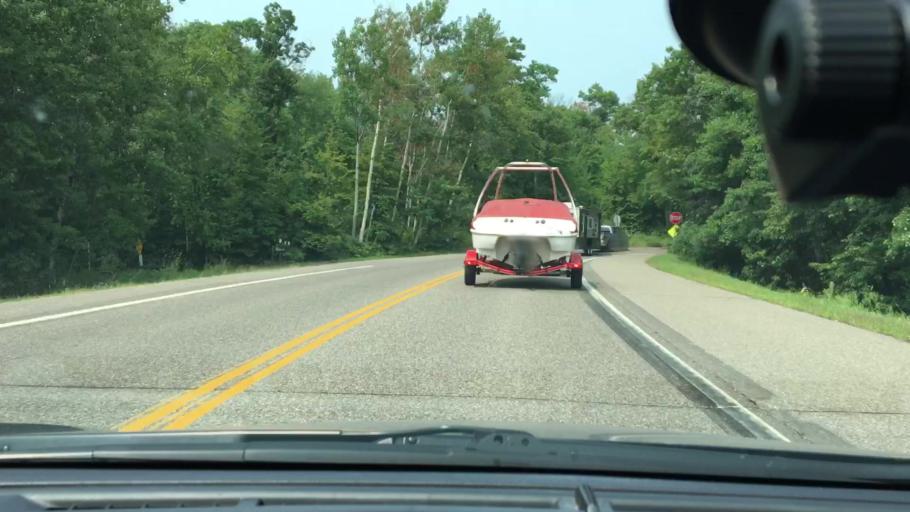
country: US
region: Minnesota
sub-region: Cass County
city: East Gull Lake
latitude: 46.4077
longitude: -94.3554
